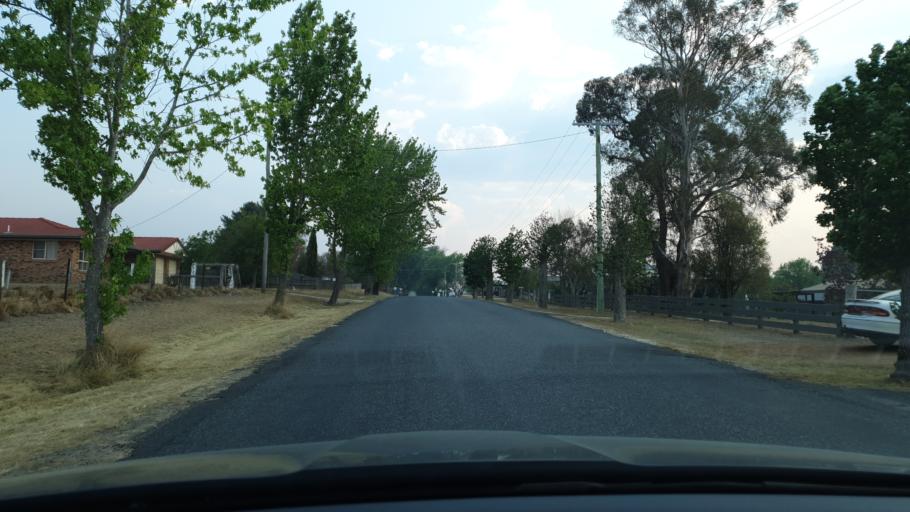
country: AU
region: New South Wales
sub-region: Tenterfield Municipality
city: Carrolls Creek
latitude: -29.0440
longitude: 152.0232
